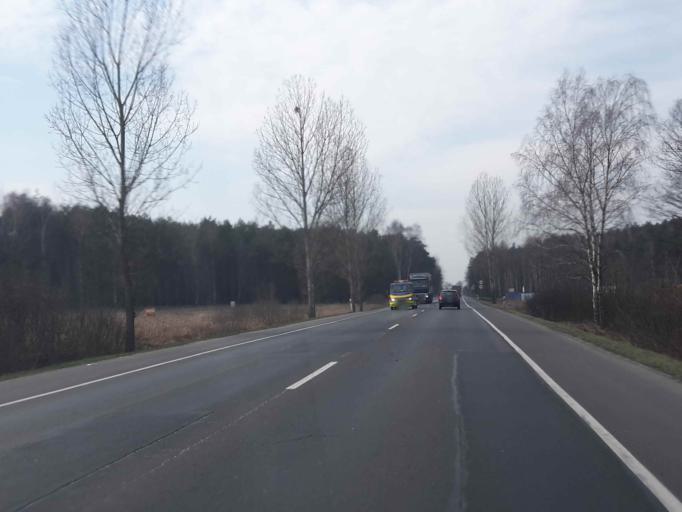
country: PL
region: Kujawsko-Pomorskie
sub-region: Powiat bydgoski
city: Biale Blota
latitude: 53.0781
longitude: 17.8534
